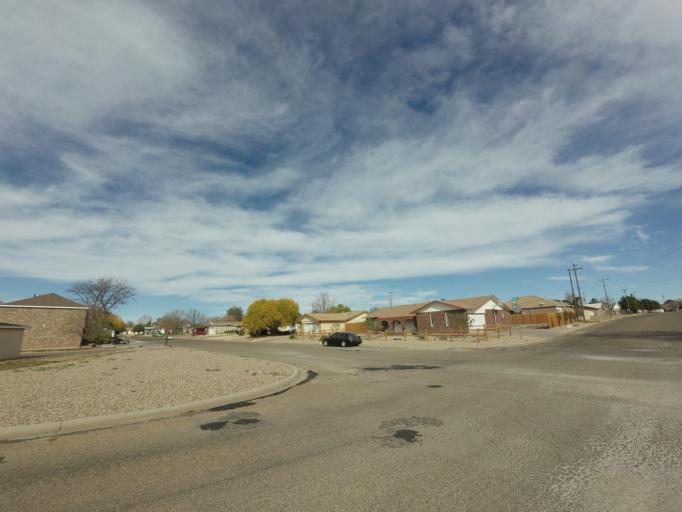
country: US
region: New Mexico
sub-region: Curry County
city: Clovis
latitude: 34.4130
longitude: -103.1919
